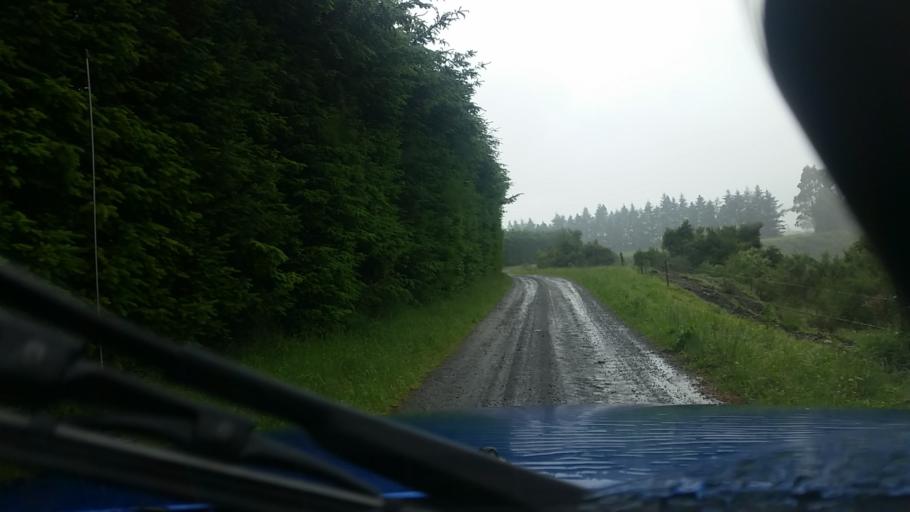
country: NZ
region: Canterbury
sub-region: Ashburton District
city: Methven
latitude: -43.5724
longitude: 171.5224
